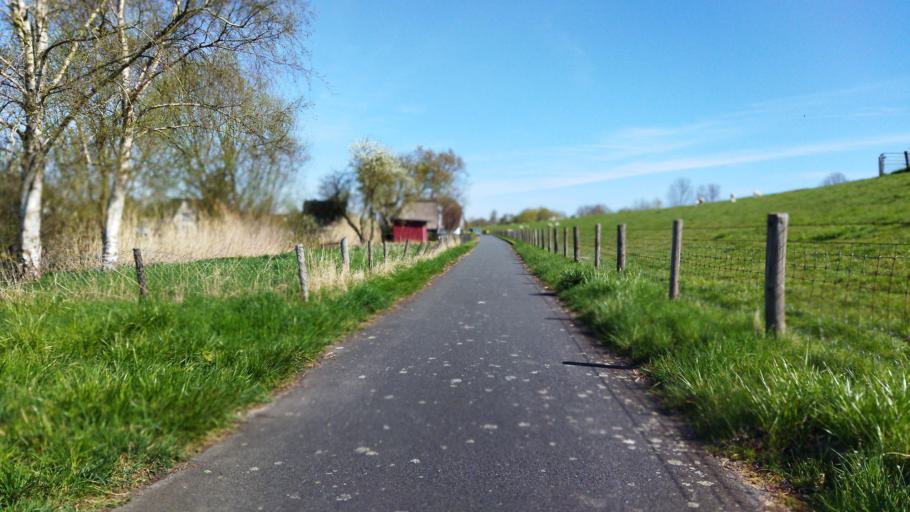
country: DE
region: Lower Saxony
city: Elsfleth
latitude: 53.2558
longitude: 8.4749
